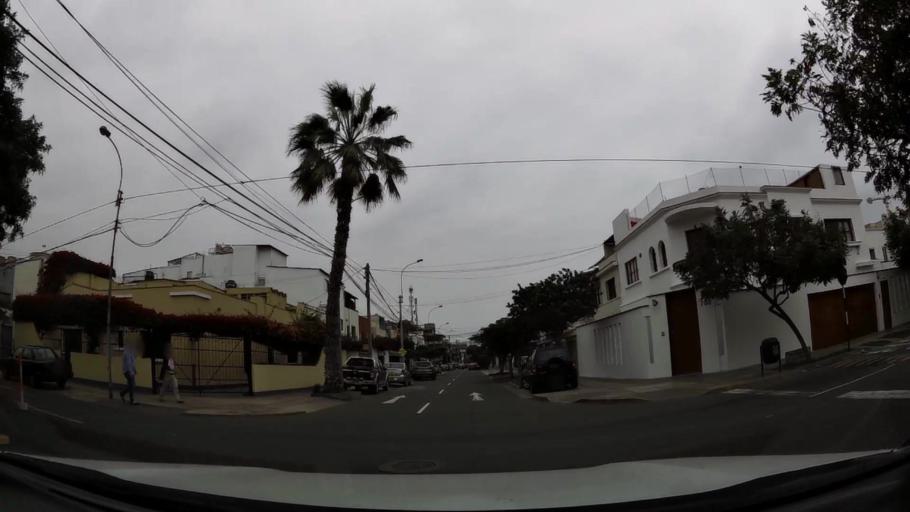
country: PE
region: Lima
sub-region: Lima
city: Surco
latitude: -12.1292
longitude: -77.0189
